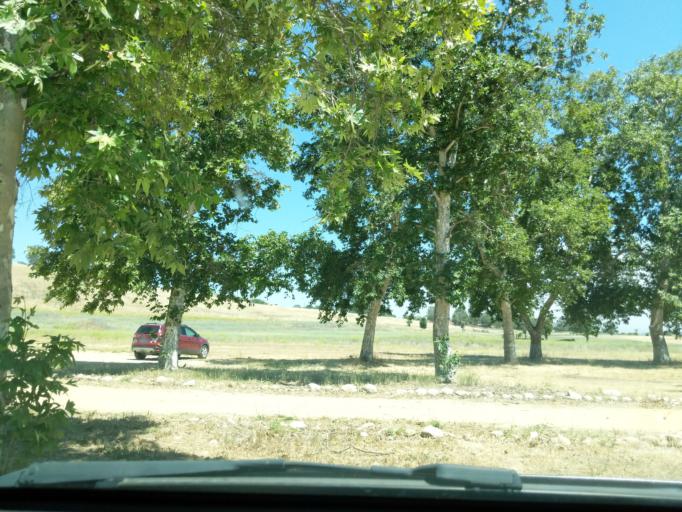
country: US
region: California
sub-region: Monterey County
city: King City
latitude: 36.0153
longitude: -121.2492
